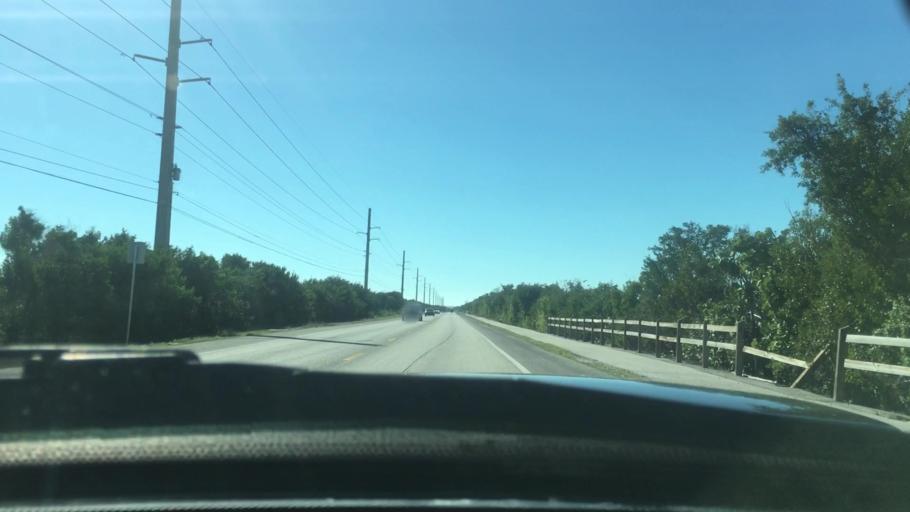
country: US
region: Florida
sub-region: Monroe County
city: Big Pine Key
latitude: 24.6687
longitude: -81.2542
